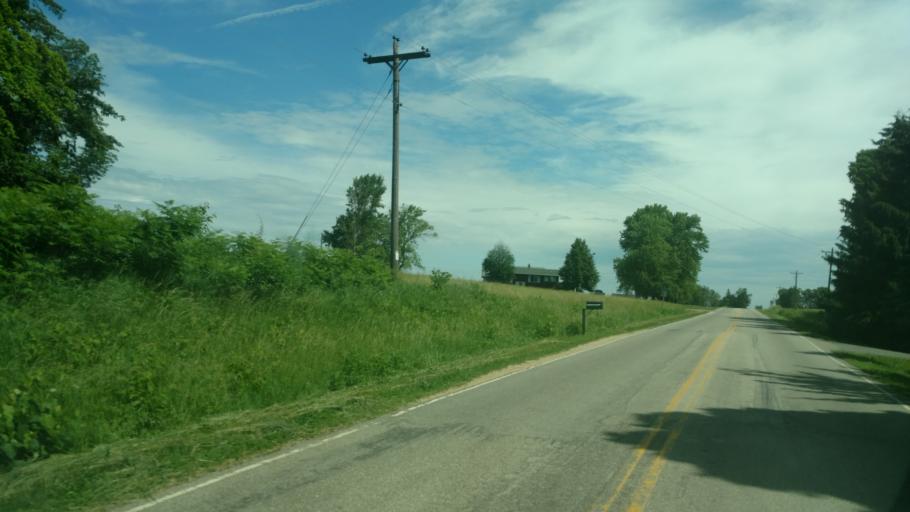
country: US
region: Wisconsin
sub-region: Vernon County
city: Hillsboro
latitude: 43.6813
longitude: -90.4522
